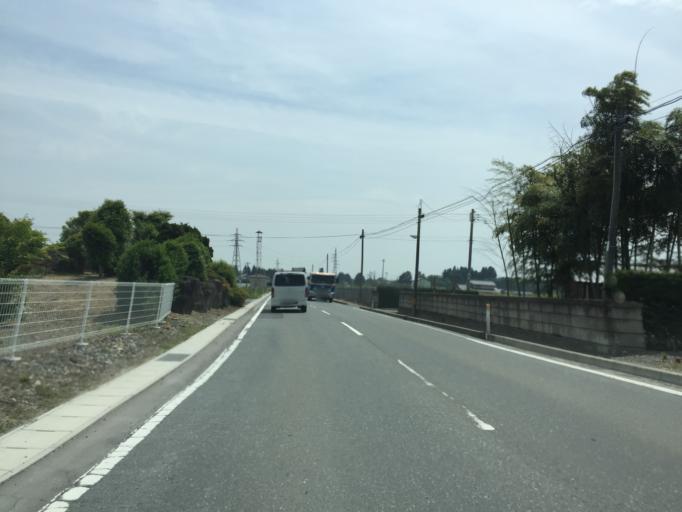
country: JP
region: Fukushima
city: Namie
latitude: 37.6325
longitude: 140.9351
